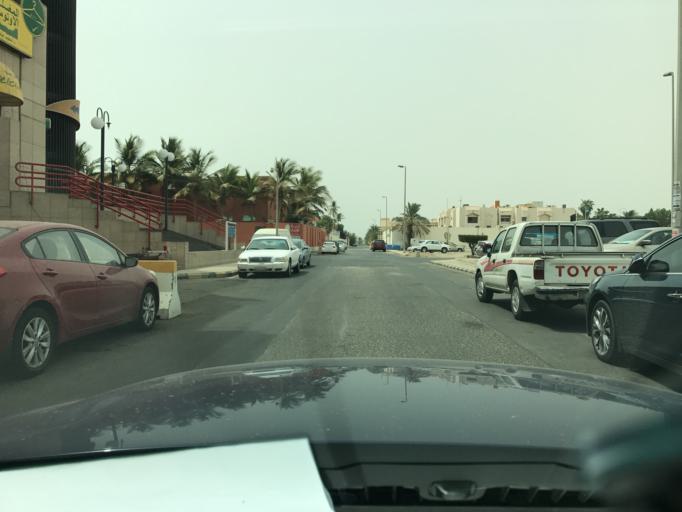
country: SA
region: Makkah
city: Jeddah
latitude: 21.5223
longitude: 39.1574
